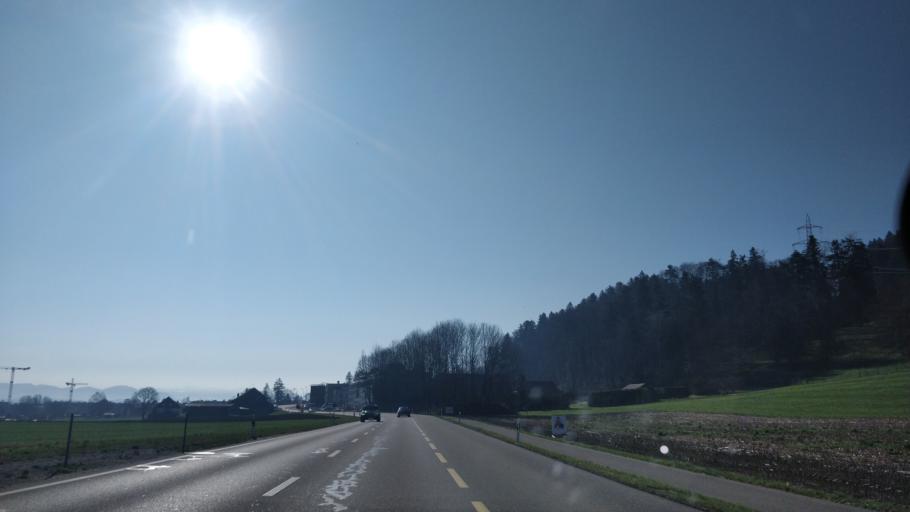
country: CH
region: Zurich
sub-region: Bezirk Uster
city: Fallanden
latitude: 47.3778
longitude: 8.6275
